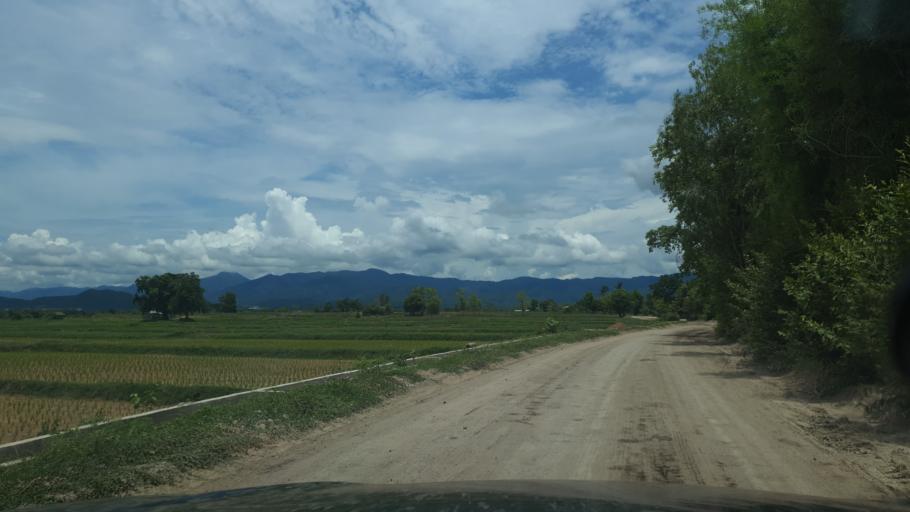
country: TH
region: Lampang
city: Sop Prap
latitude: 17.9398
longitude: 99.3565
